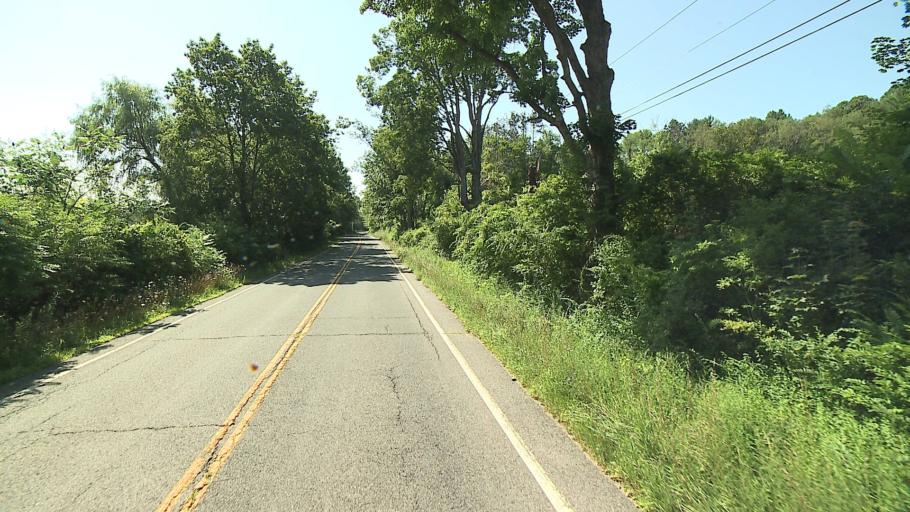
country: US
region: Massachusetts
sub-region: Berkshire County
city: Sheffield
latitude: 42.0482
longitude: -73.4254
